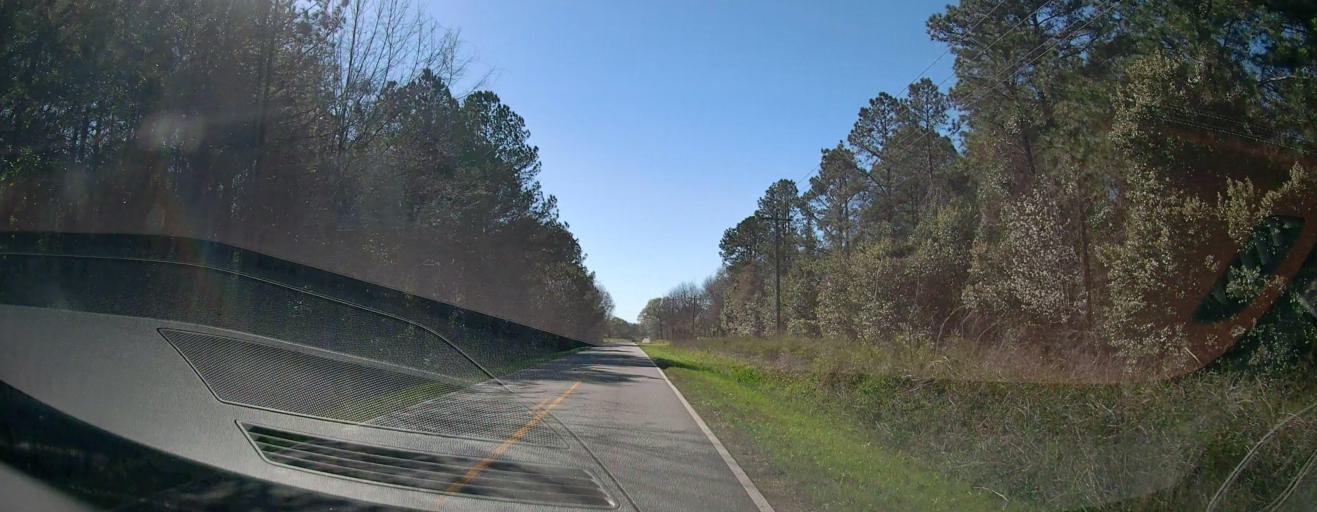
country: US
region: Georgia
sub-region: Peach County
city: Byron
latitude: 32.6444
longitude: -83.8217
